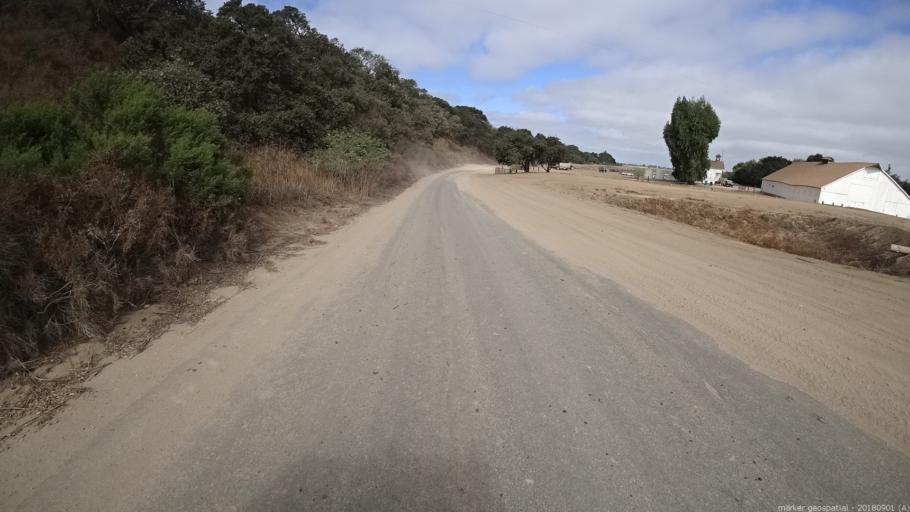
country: US
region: California
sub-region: Monterey County
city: Soledad
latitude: 36.4310
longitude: -121.4040
